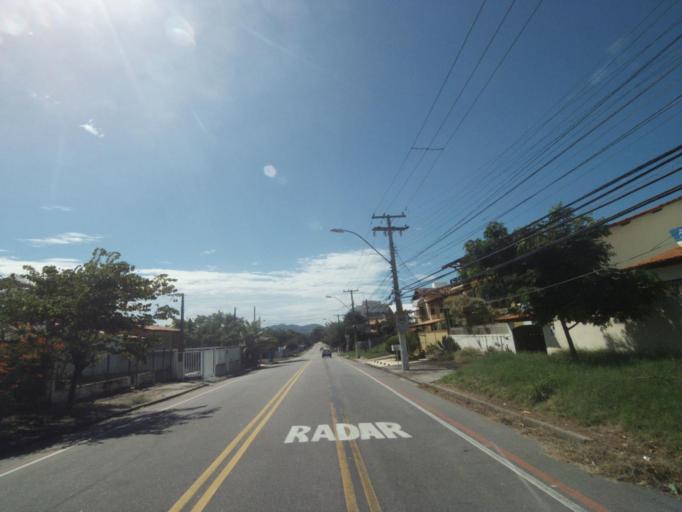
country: BR
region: Rio de Janeiro
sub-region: Niteroi
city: Niteroi
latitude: -22.9523
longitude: -43.0845
